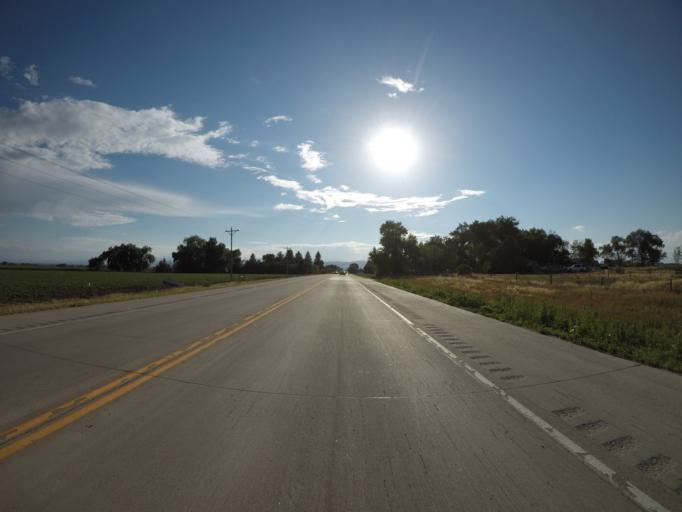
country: US
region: Colorado
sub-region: Weld County
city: Severance
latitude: 40.5809
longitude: -104.9504
